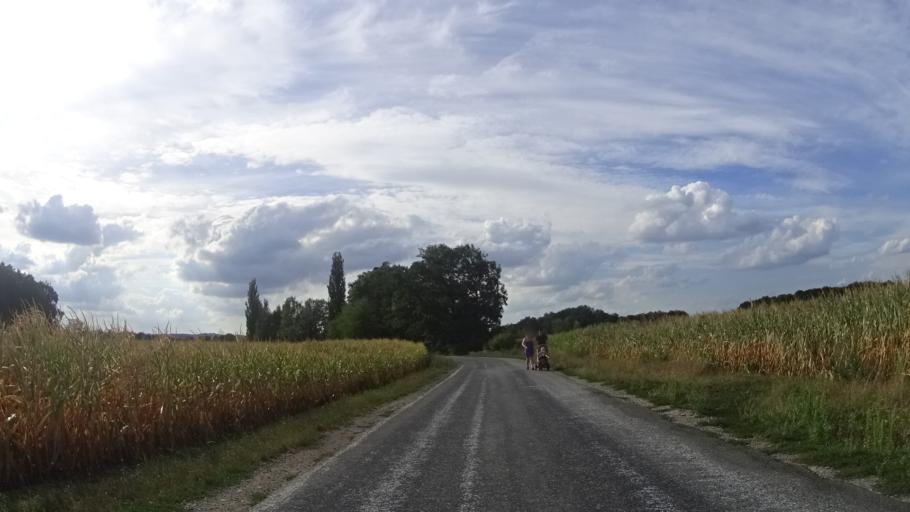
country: CZ
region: Olomoucky
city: Dubicko
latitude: 49.7994
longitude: 16.9552
